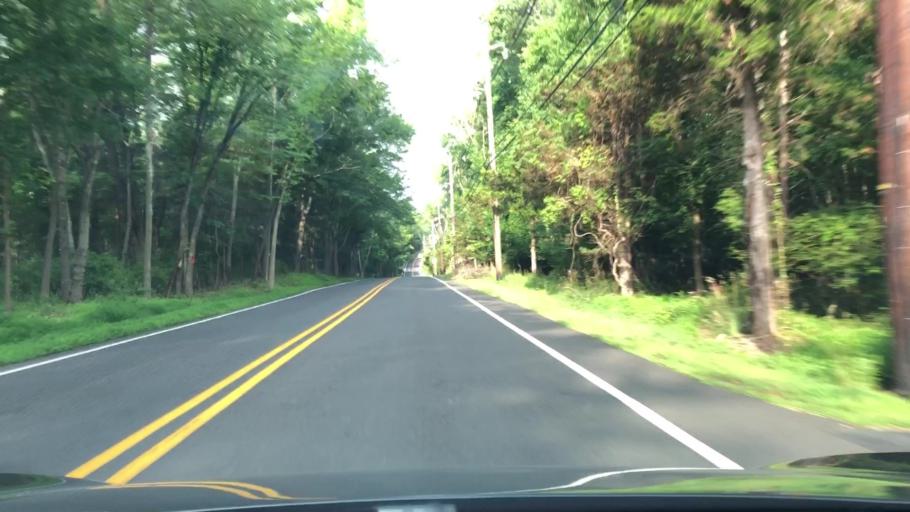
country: US
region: New Jersey
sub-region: Mercer County
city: Lawrenceville
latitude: 40.3420
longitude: -74.7397
